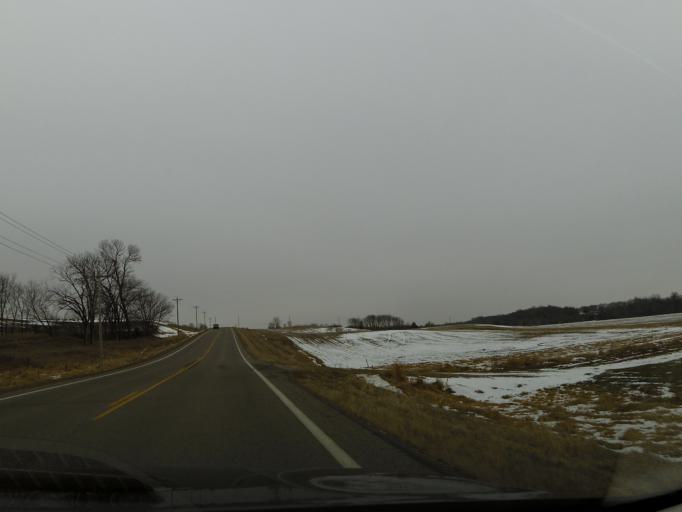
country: US
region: Minnesota
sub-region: Scott County
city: Jordan
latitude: 44.6306
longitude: -93.5709
